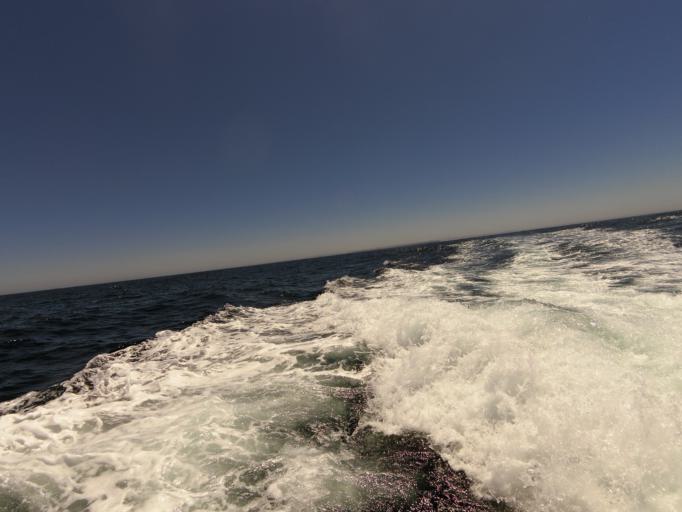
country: PT
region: Leiria
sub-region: Peniche
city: Peniche
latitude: 39.3921
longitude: -9.4751
